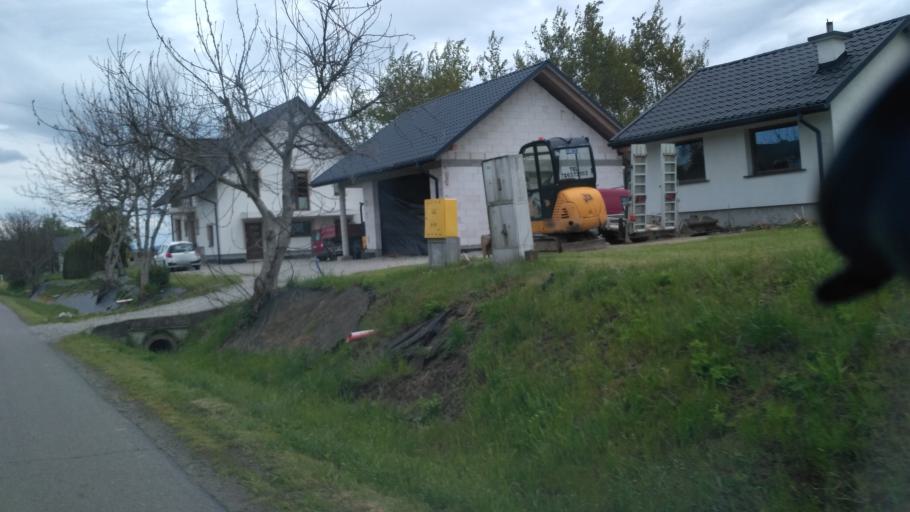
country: PL
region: Subcarpathian Voivodeship
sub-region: Powiat przeworski
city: Jawornik Polski
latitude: 49.8368
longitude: 22.2968
